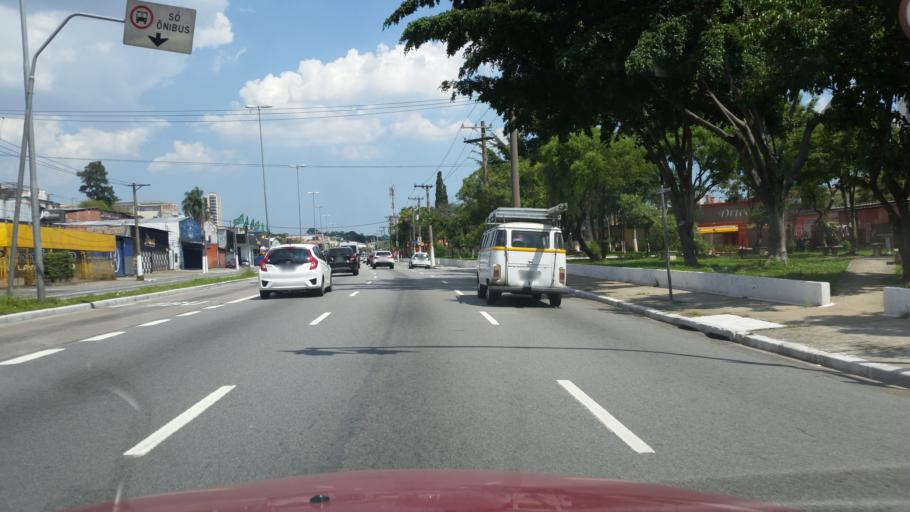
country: BR
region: Sao Paulo
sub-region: Diadema
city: Diadema
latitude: -23.6554
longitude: -46.6667
